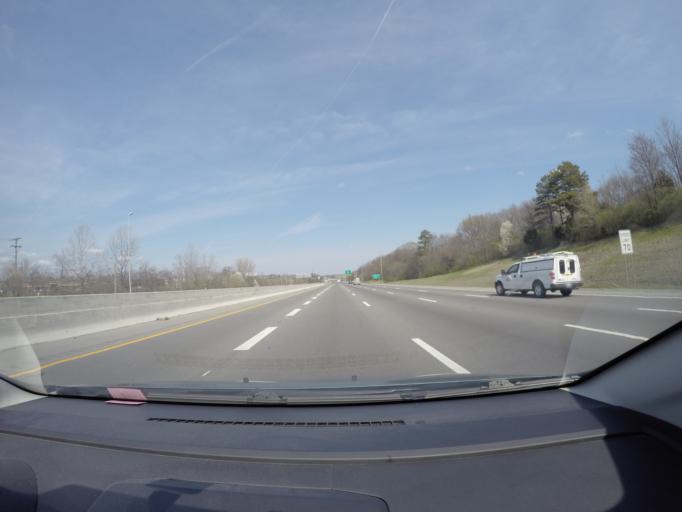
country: US
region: Tennessee
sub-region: Davidson County
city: Oak Hill
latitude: 36.0761
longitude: -86.6937
